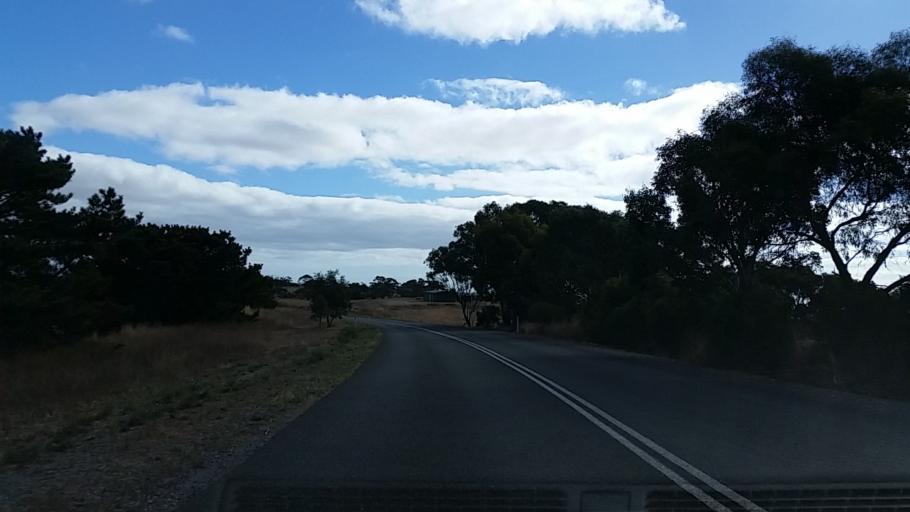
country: AU
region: South Australia
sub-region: Yankalilla
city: Normanville
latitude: -35.4083
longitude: 138.4023
